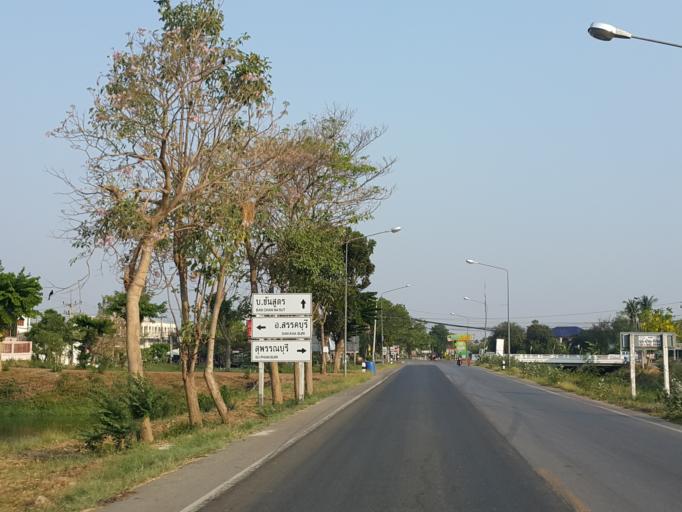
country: TH
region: Chai Nat
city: Sankhaburi
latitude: 15.0483
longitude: 100.1579
